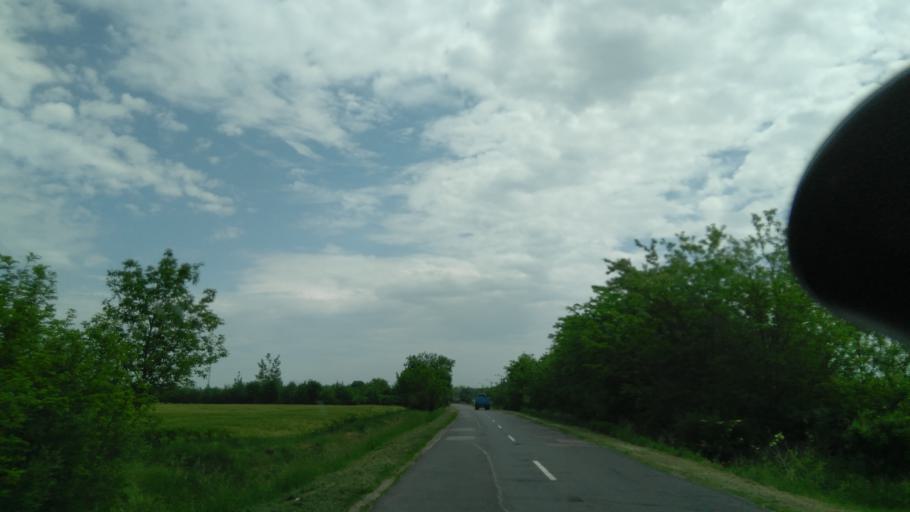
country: HU
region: Hajdu-Bihar
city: Komadi
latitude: 47.0189
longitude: 21.5814
